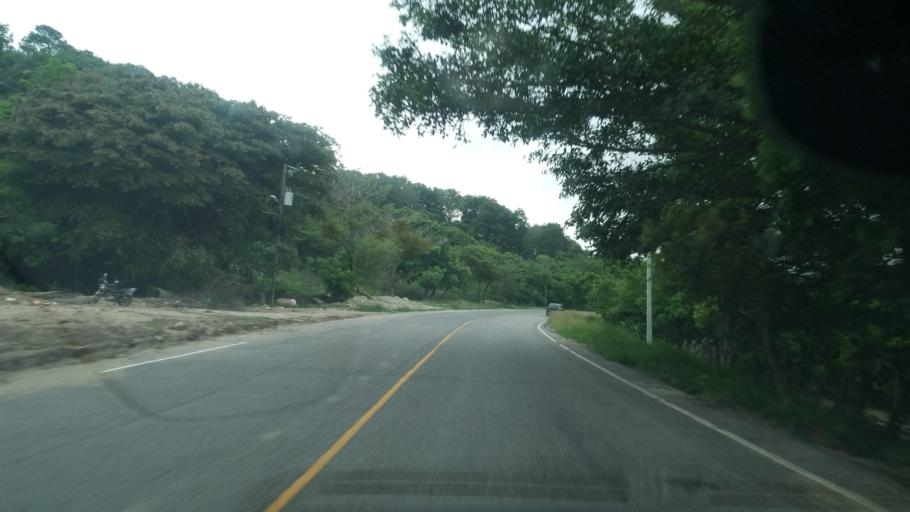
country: HN
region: Ocotepeque
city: Sinuapa
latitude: 14.5021
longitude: -89.2253
